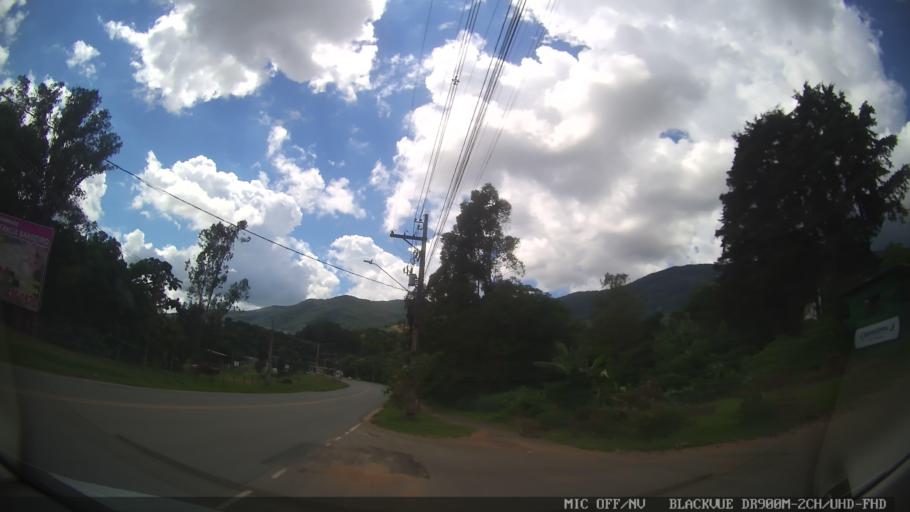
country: BR
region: Minas Gerais
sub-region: Extrema
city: Extrema
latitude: -22.8645
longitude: -46.3387
